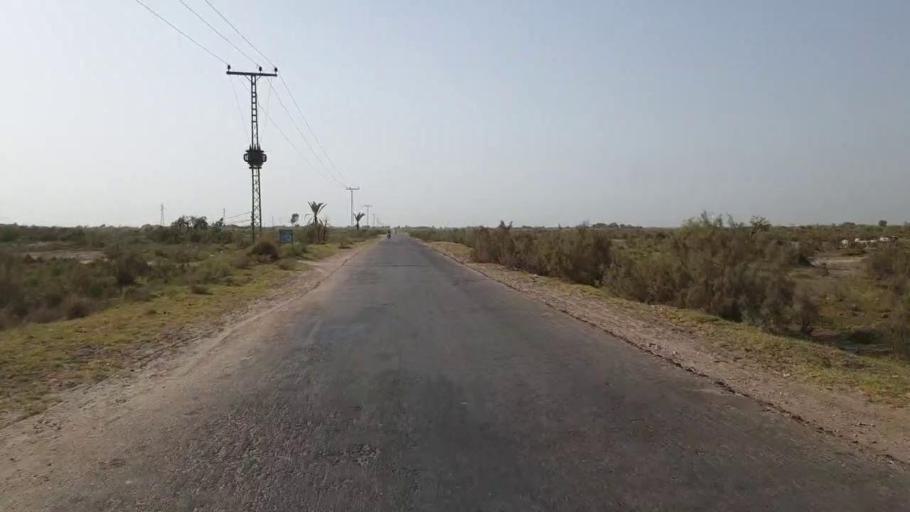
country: PK
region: Sindh
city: Khadro
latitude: 26.3466
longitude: 68.9242
